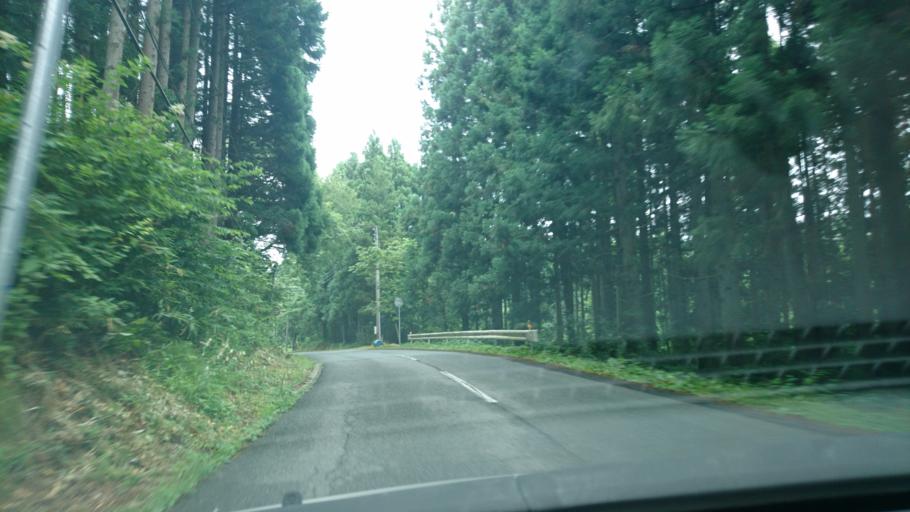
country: JP
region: Iwate
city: Ichinoseki
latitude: 38.9039
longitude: 141.1166
